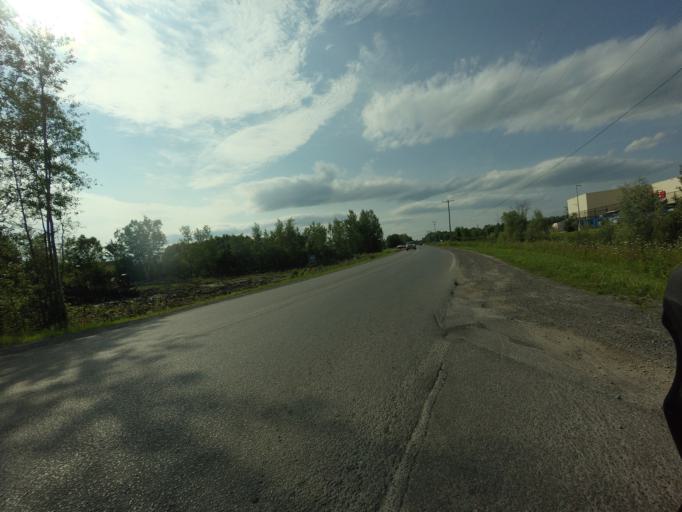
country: CA
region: Ontario
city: Prescott
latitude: 45.0276
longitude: -75.6343
